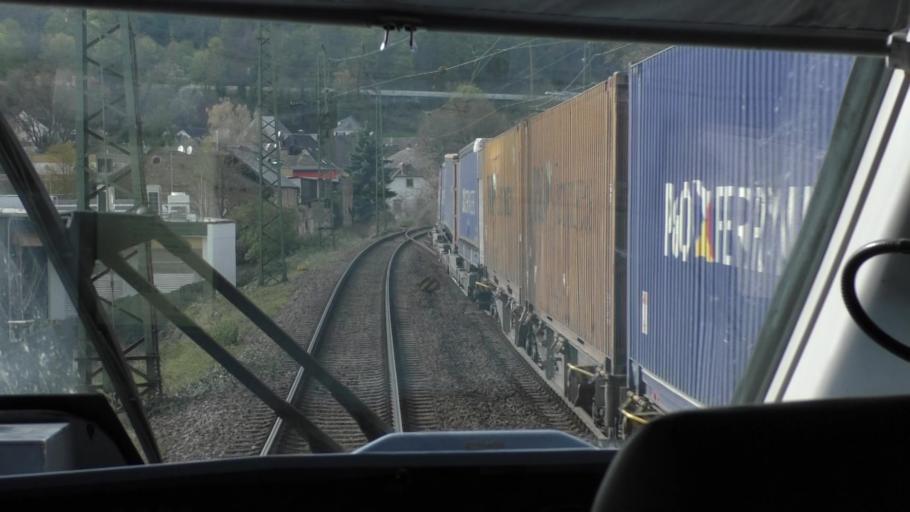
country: DE
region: Rheinland-Pfalz
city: Andernach
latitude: 50.4359
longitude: 7.4004
